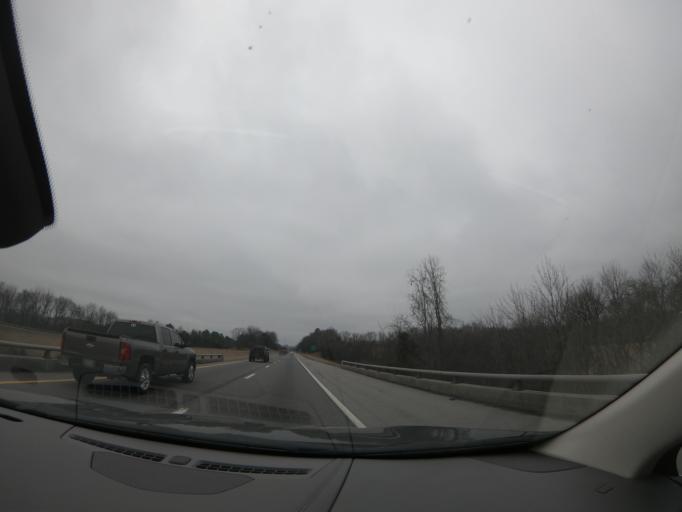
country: US
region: Tennessee
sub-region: Rutherford County
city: Plainview
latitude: 35.6076
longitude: -86.2397
